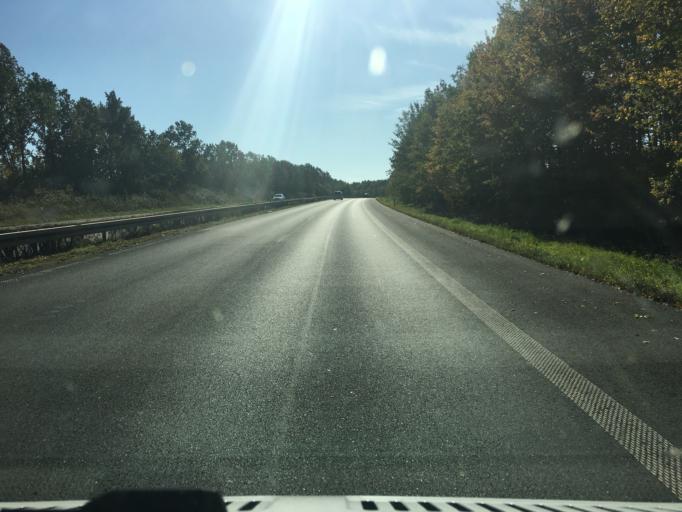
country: DE
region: Saxony
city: Dennheritz
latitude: 50.8031
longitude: 12.4550
